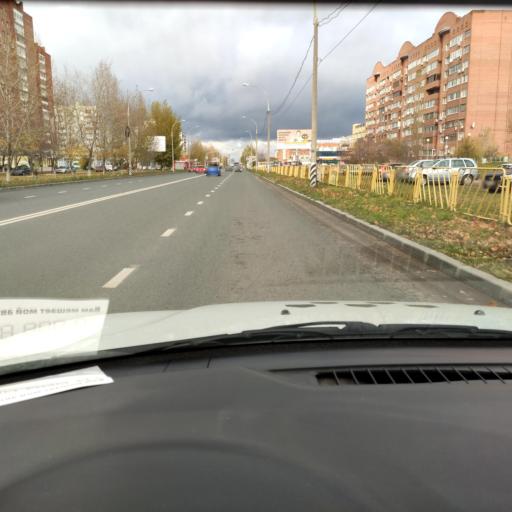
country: RU
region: Samara
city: Tol'yatti
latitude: 53.5424
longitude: 49.3458
